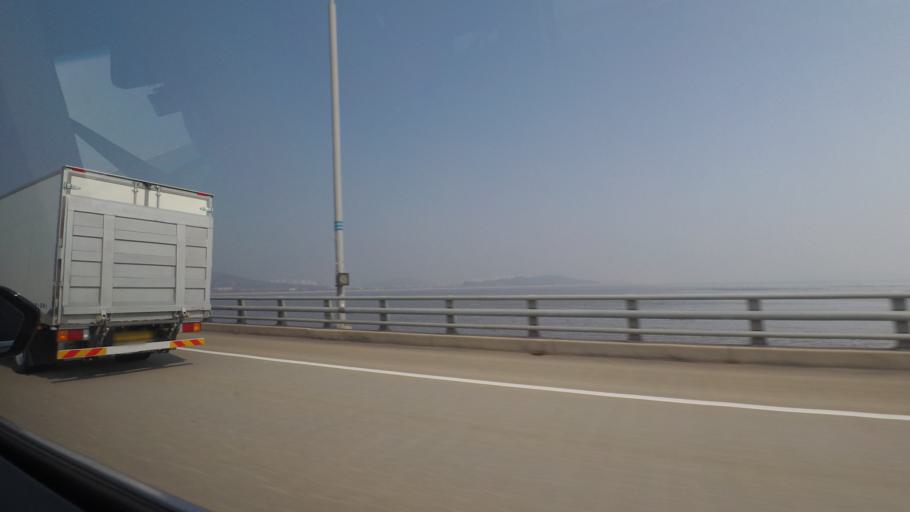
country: KR
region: Incheon
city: Incheon
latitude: 37.4552
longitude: 126.5246
